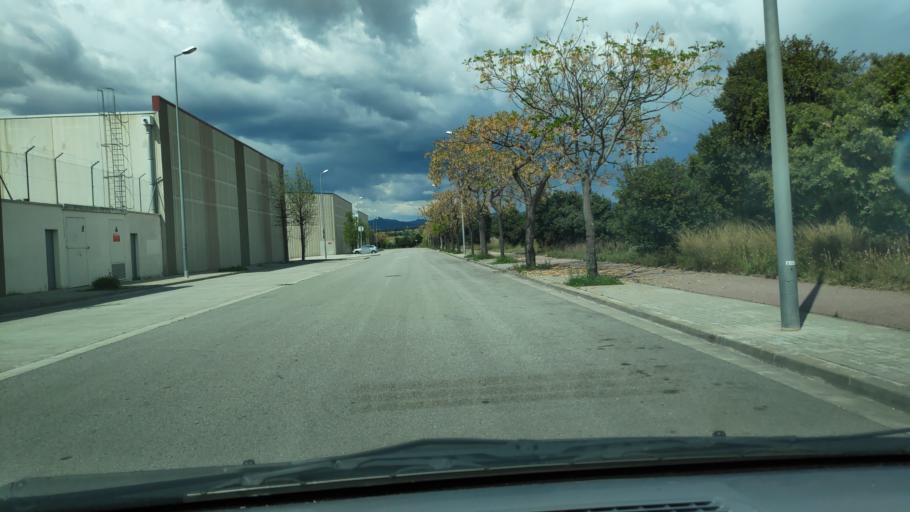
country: ES
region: Catalonia
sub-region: Provincia de Barcelona
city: Polinya
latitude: 41.5410
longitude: 2.1379
